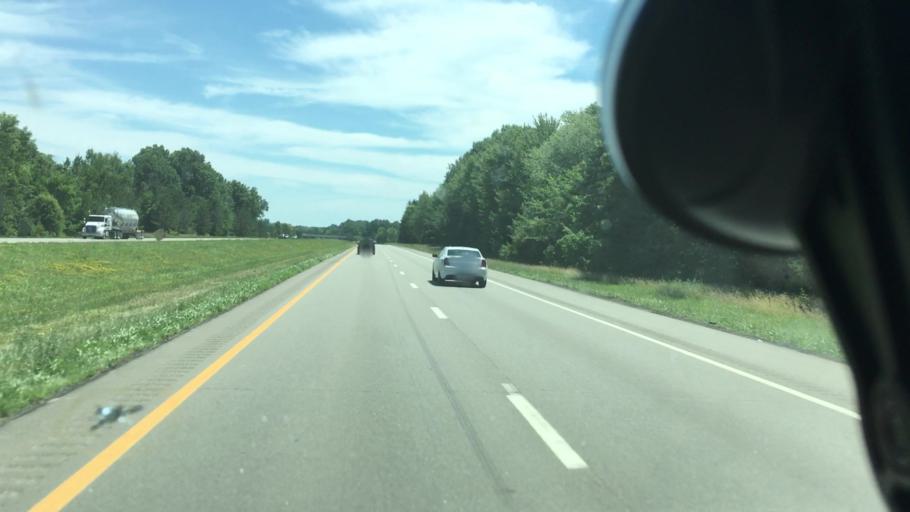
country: US
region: Ohio
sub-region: Mahoning County
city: Austintown
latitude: 41.0787
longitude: -80.7525
